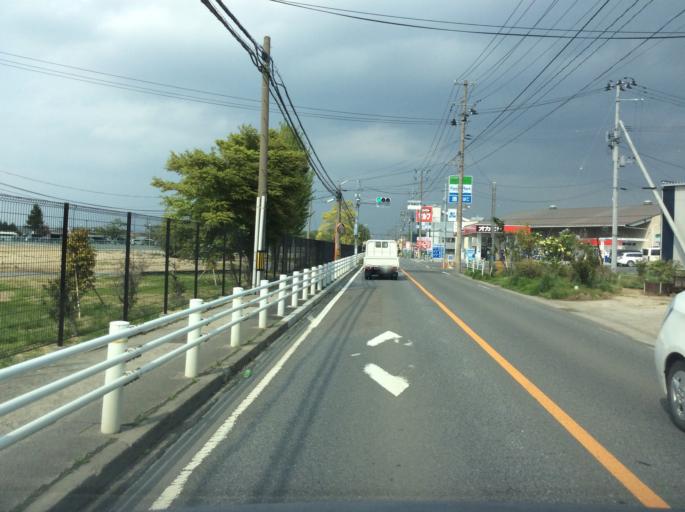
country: JP
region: Fukushima
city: Koriyama
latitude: 37.4156
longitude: 140.4002
